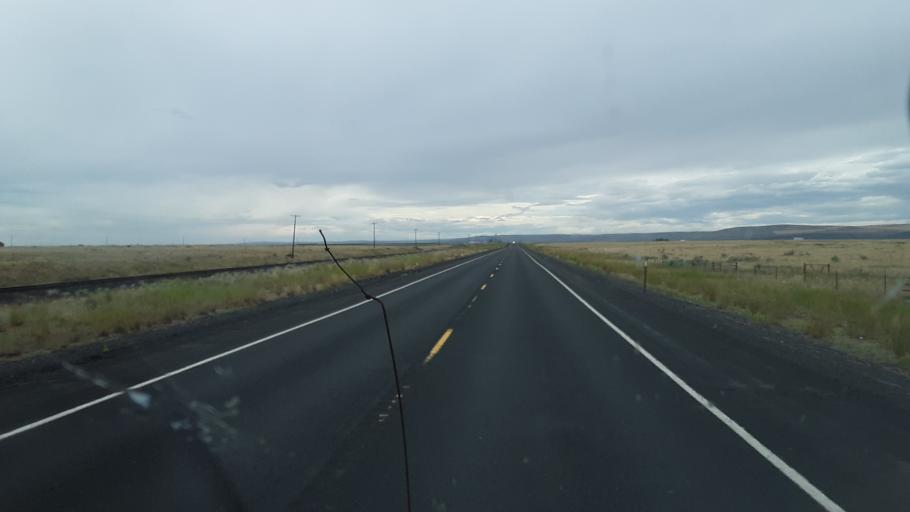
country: US
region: Washington
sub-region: Okanogan County
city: Coulee Dam
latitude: 47.6615
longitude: -119.2066
